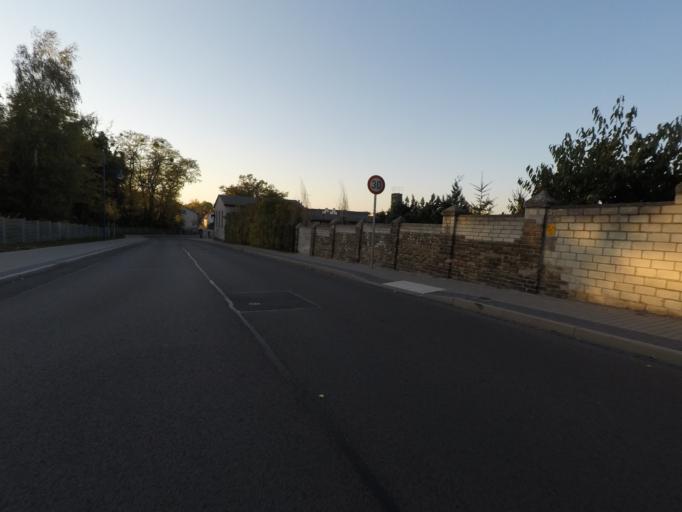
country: DE
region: Brandenburg
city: Melchow
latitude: 52.8391
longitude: 13.7355
